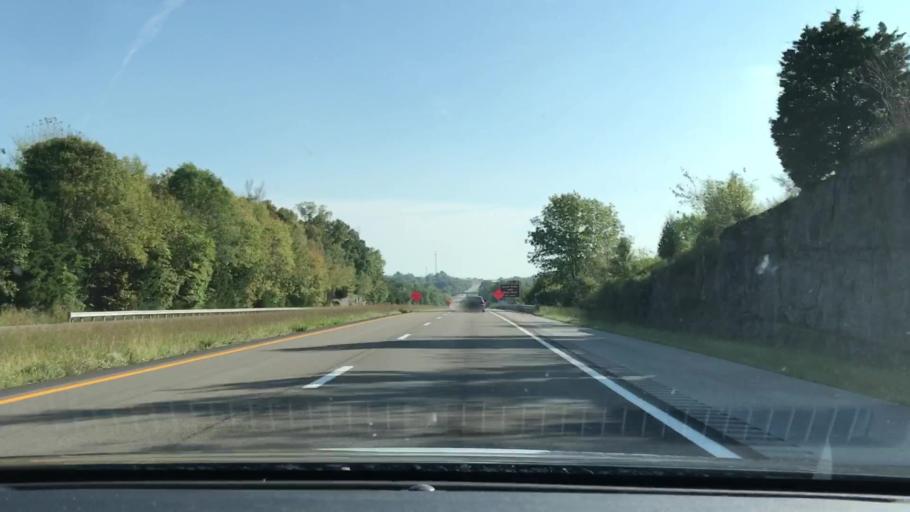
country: US
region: Kentucky
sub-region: Adair County
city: Columbia
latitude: 37.0782
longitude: -85.3245
